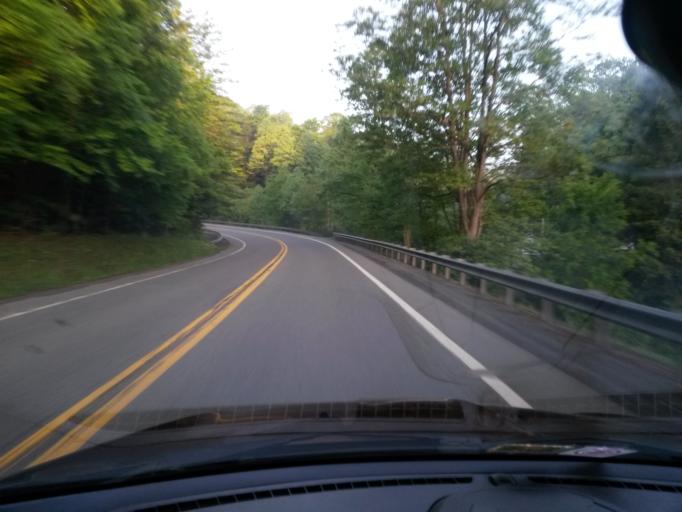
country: US
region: West Virginia
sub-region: Wyoming County
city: Pineville
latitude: 37.6398
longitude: -81.4682
